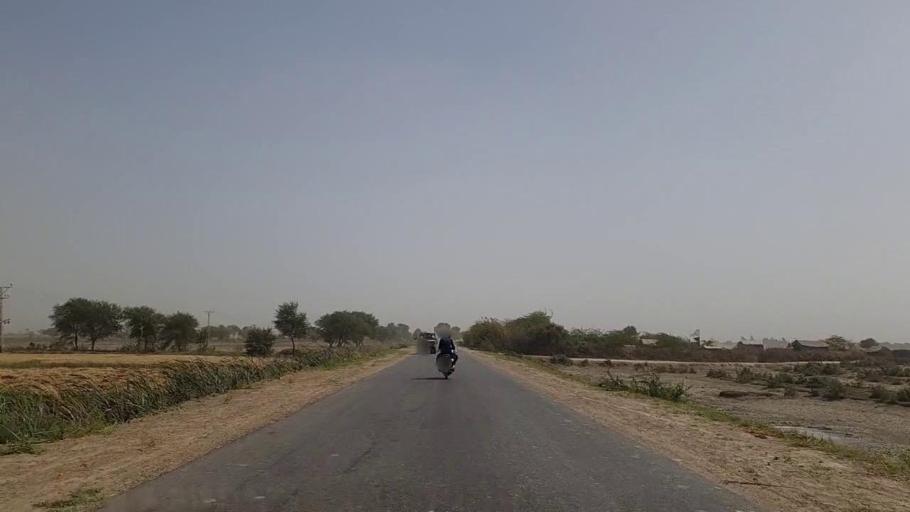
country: PK
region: Sindh
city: Talhar
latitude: 24.8747
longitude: 68.8370
